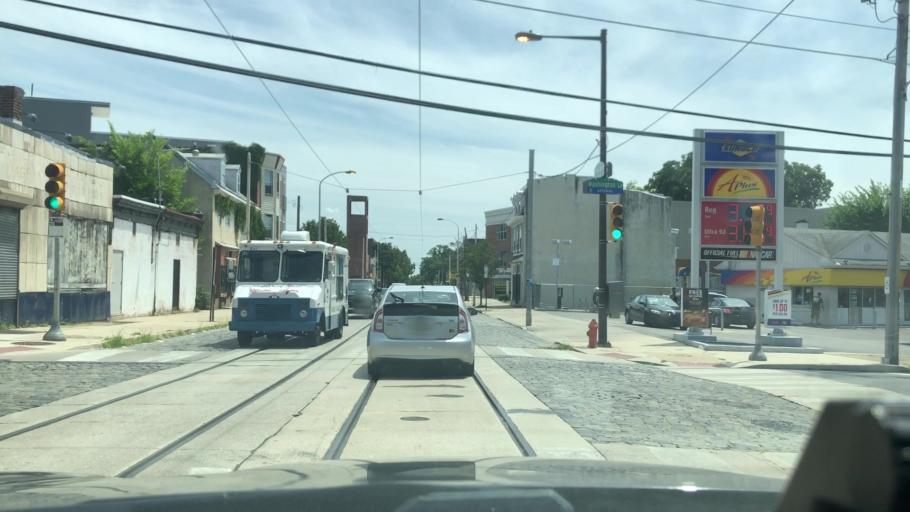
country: US
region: Pennsylvania
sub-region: Montgomery County
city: Wyndmoor
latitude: 40.0433
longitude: -75.1810
